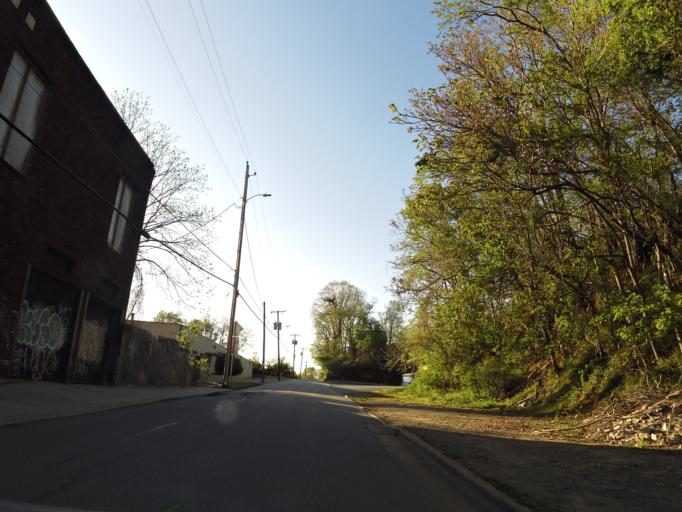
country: US
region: North Carolina
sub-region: Buncombe County
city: Asheville
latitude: 35.5874
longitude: -82.5671
